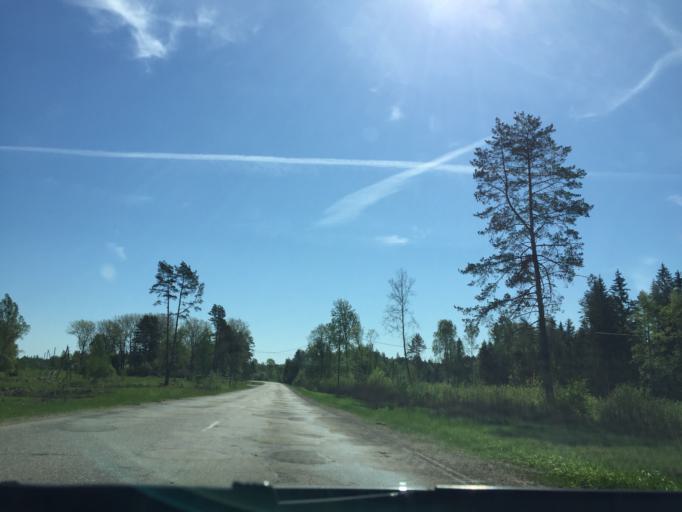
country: LV
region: Ropazu
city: Ropazi
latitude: 57.0078
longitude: 24.5696
